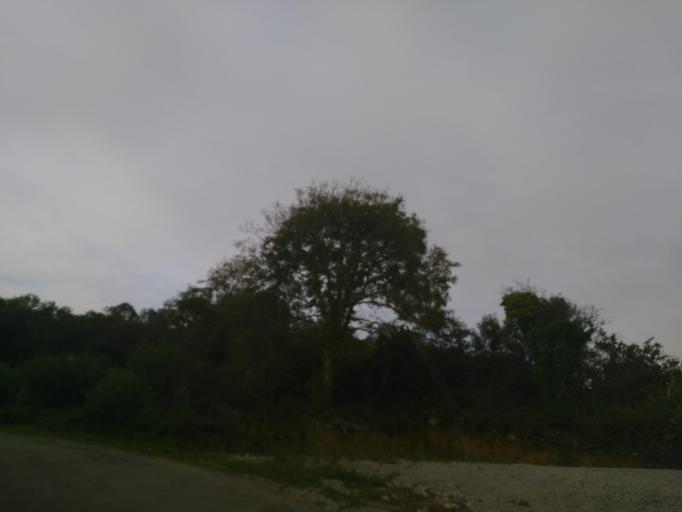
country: FR
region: Brittany
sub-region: Departement du Finistere
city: Crozon
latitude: 48.2385
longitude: -4.4423
